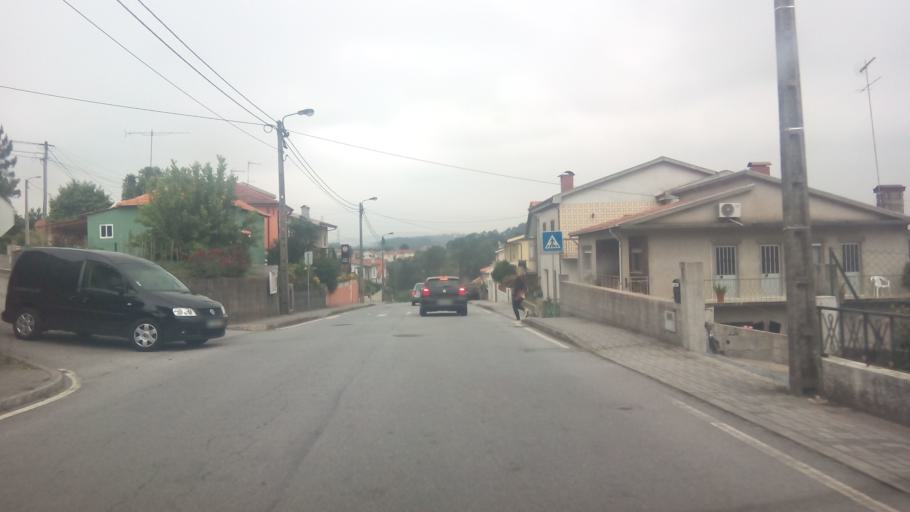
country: PT
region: Porto
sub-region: Paredes
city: Baltar
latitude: 41.1804
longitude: -8.3486
